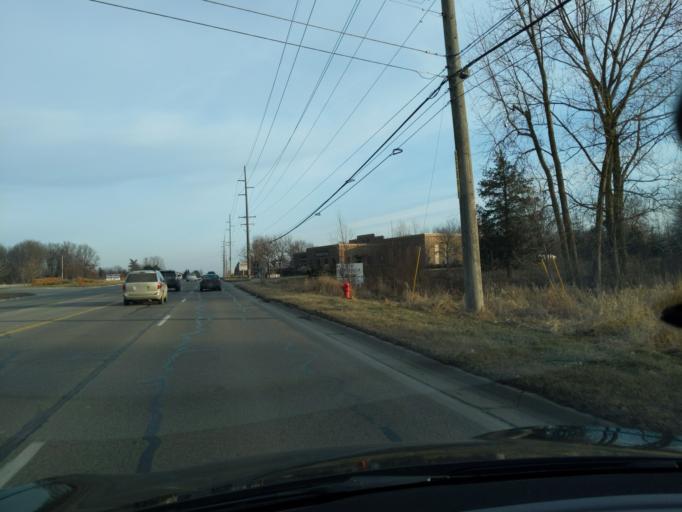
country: US
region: Michigan
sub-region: Livingston County
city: Brighton
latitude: 42.5726
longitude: -83.8279
